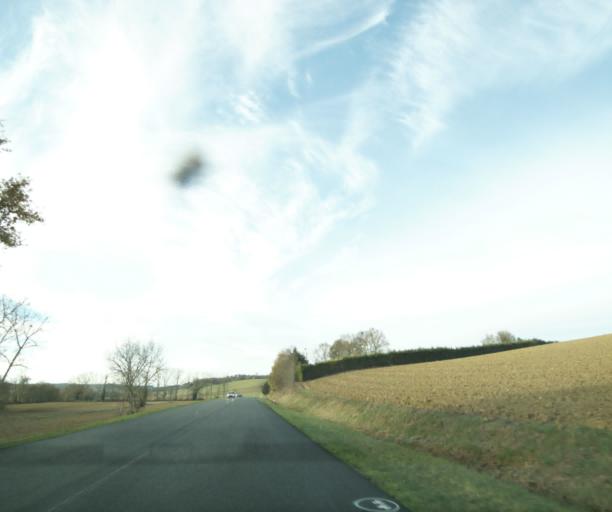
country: FR
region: Midi-Pyrenees
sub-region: Departement du Gers
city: Jegun
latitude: 43.6887
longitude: 0.4815
